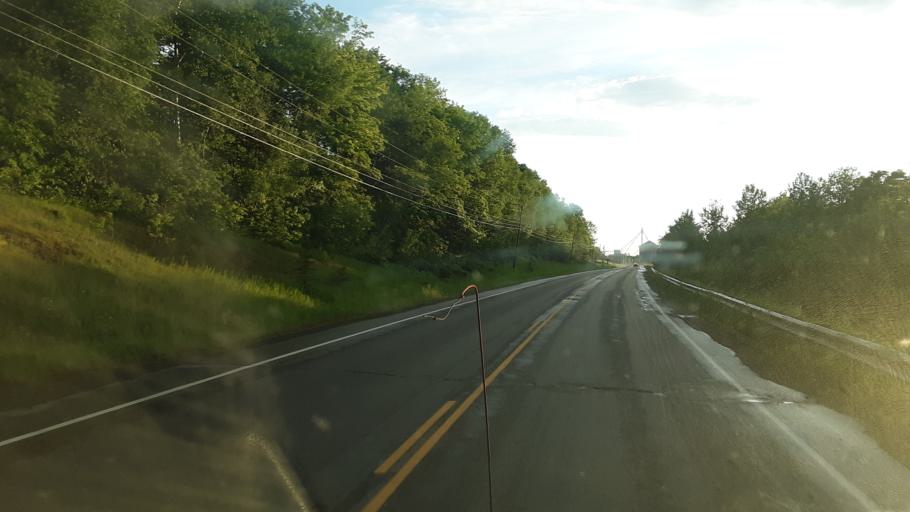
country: US
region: Maine
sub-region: Aroostook County
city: Presque Isle
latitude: 46.6940
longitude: -67.9892
